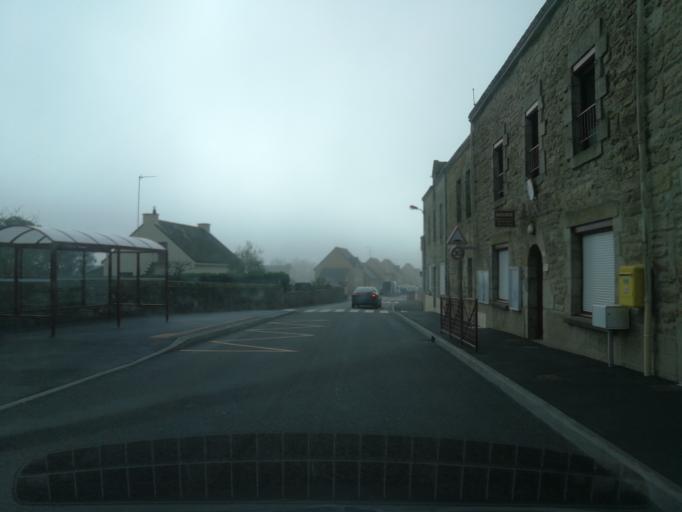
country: FR
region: Brittany
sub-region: Departement du Morbihan
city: La Vraie-Croix
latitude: 47.7418
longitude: -2.5011
